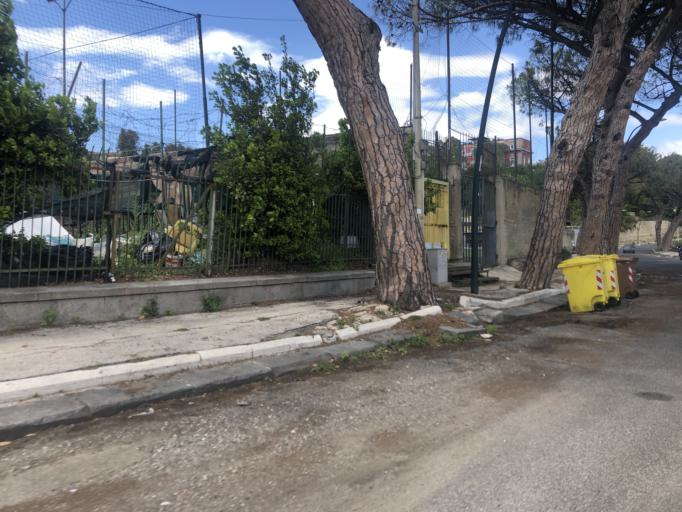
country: IT
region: Campania
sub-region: Provincia di Napoli
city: Bagnoli
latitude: 40.7997
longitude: 14.1874
